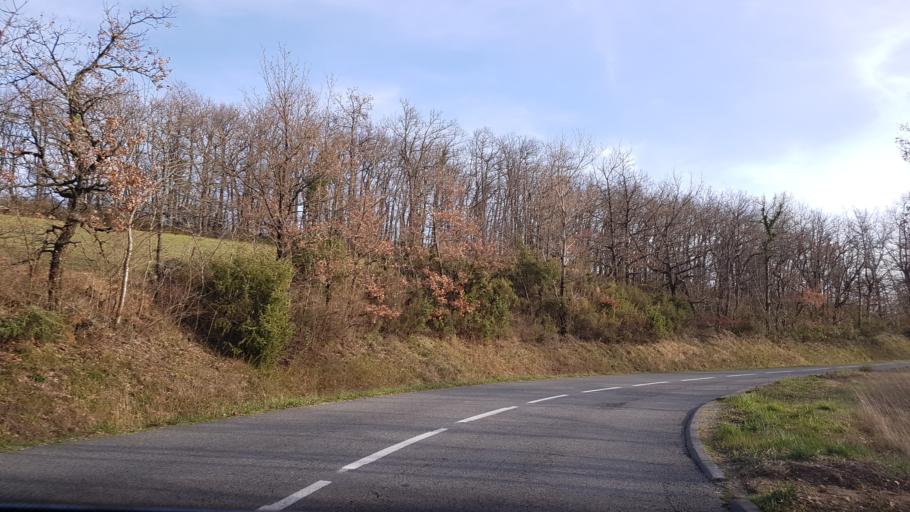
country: FR
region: Languedoc-Roussillon
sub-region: Departement de l'Aude
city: Villeneuve-la-Comptal
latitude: 43.2392
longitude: 1.9175
